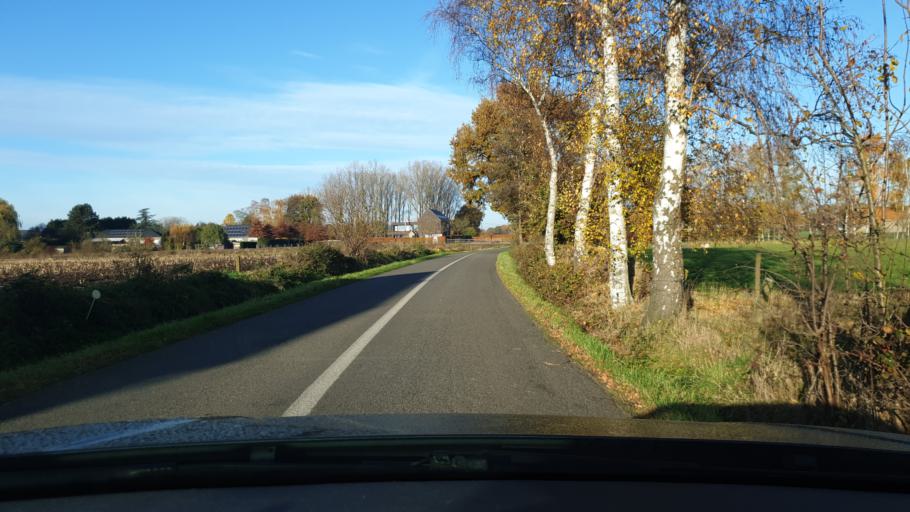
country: BE
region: Flanders
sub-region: Provincie Antwerpen
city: Geel
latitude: 51.1457
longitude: 4.9813
